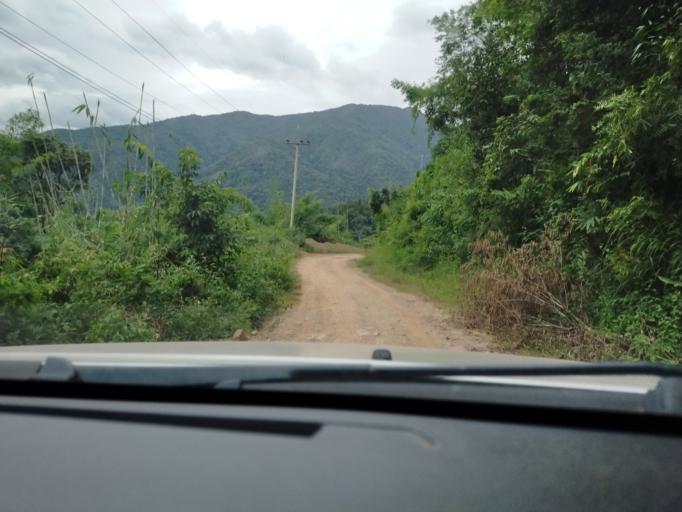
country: TH
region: Nan
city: Chaloem Phra Kiat
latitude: 19.8069
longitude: 101.3619
